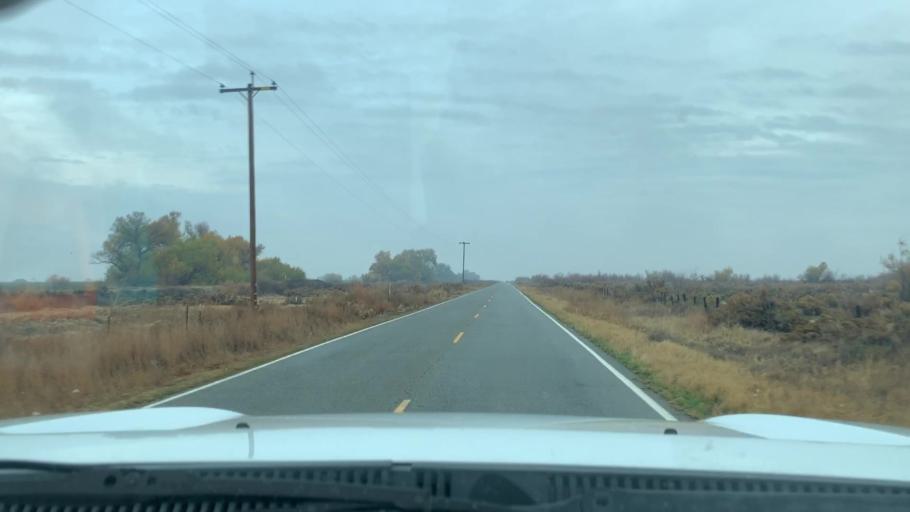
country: US
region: California
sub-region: Kern County
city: Lost Hills
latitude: 35.7229
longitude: -119.5795
